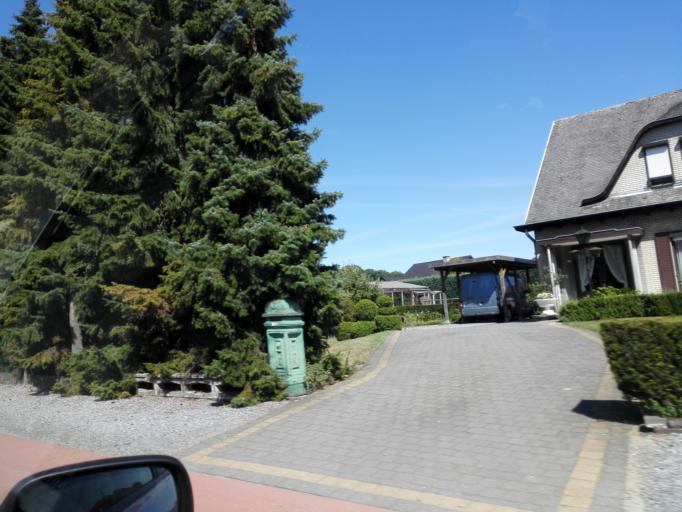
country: BE
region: Flanders
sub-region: Provincie Limburg
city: Opglabbeek
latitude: 51.0500
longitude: 5.5863
